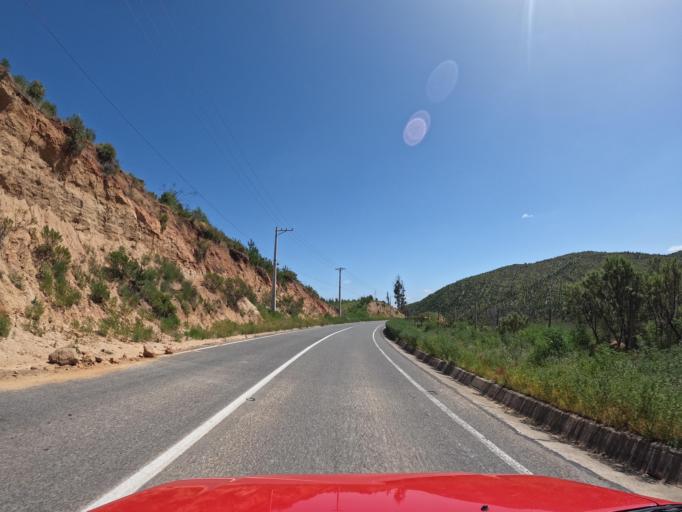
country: CL
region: O'Higgins
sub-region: Provincia de Colchagua
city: Santa Cruz
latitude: -34.6736
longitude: -71.8124
